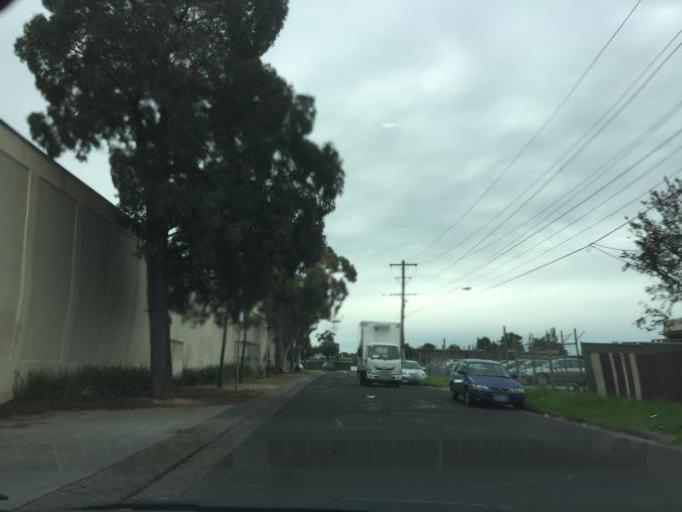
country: AU
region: Victoria
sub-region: Brimbank
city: Sunshine North
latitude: -37.7827
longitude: 144.8347
